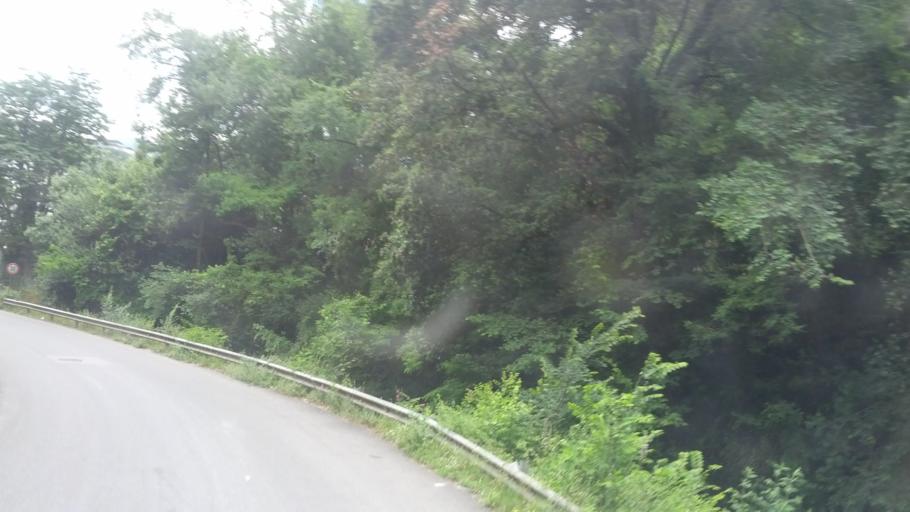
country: IT
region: Tuscany
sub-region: Provincia di Massa-Carrara
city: Carrara
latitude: 44.0847
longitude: 10.1029
